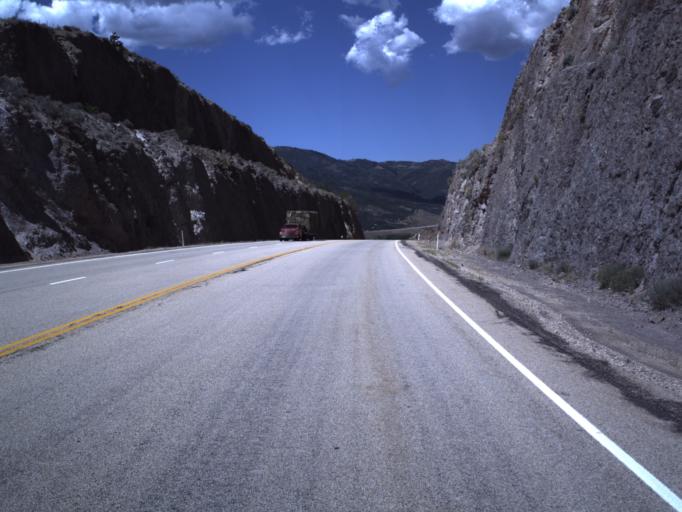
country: US
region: Utah
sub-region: Wasatch County
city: Heber
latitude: 40.5911
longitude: -111.3908
